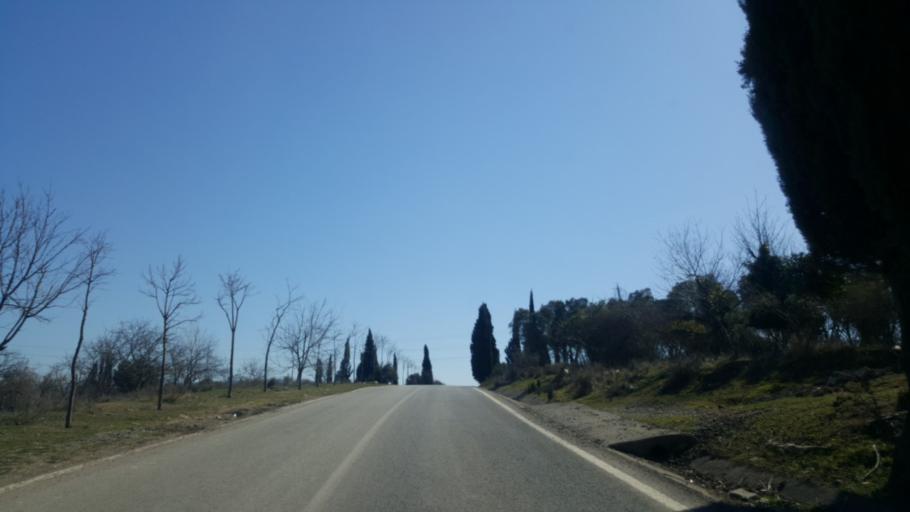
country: TR
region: Kocaeli
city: Tavsancil
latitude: 40.7849
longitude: 29.5732
